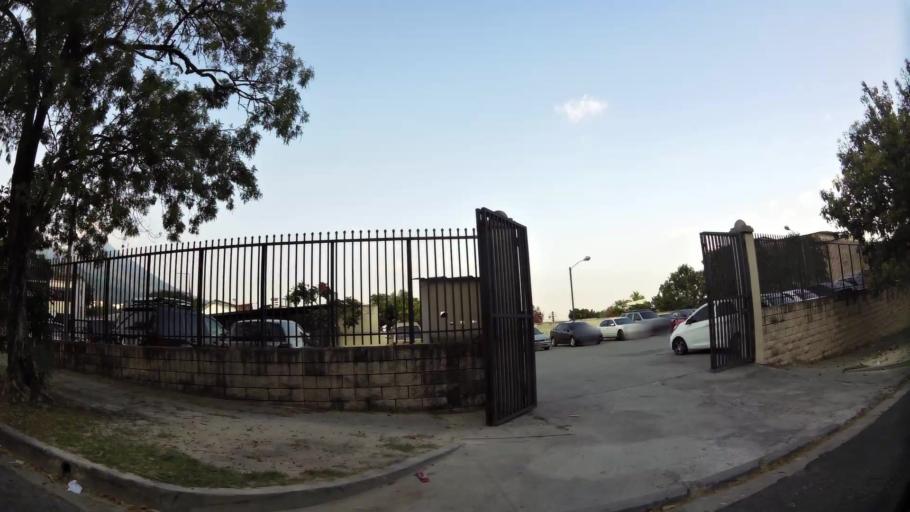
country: SV
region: La Libertad
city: Antiguo Cuscatlan
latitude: 13.6999
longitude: -89.2494
